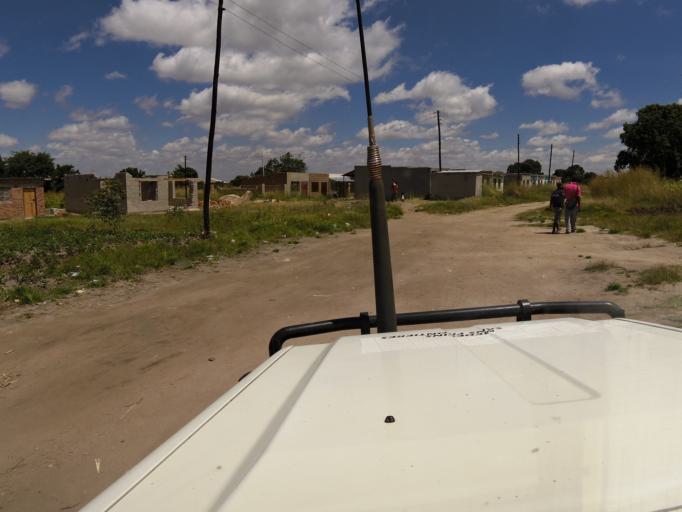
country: ZW
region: Harare
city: Epworth
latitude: -17.9052
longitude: 31.1557
